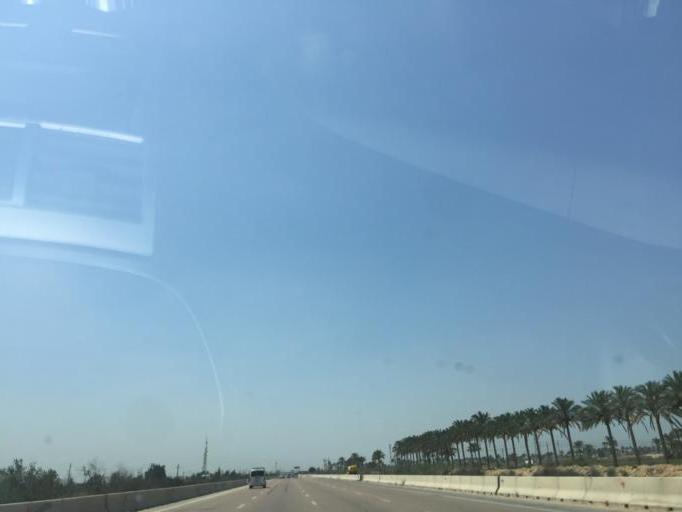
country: EG
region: Al Buhayrah
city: Abu al Matamir
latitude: 30.7709
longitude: 29.9749
